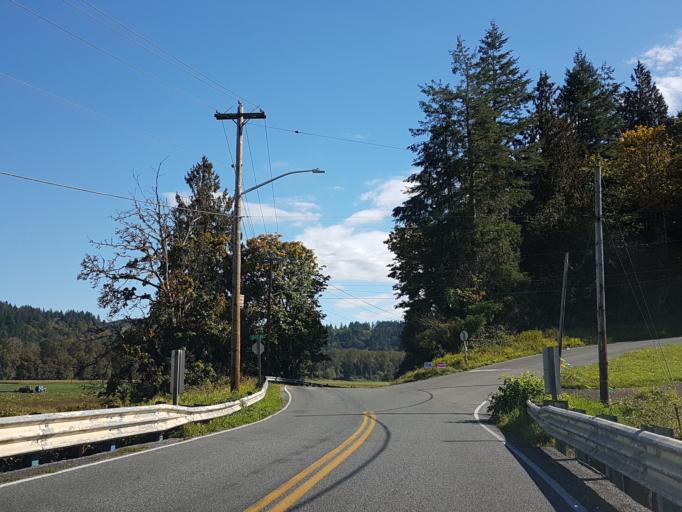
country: US
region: Washington
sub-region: Snohomish County
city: Cathcart
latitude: 47.8418
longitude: -122.0815
